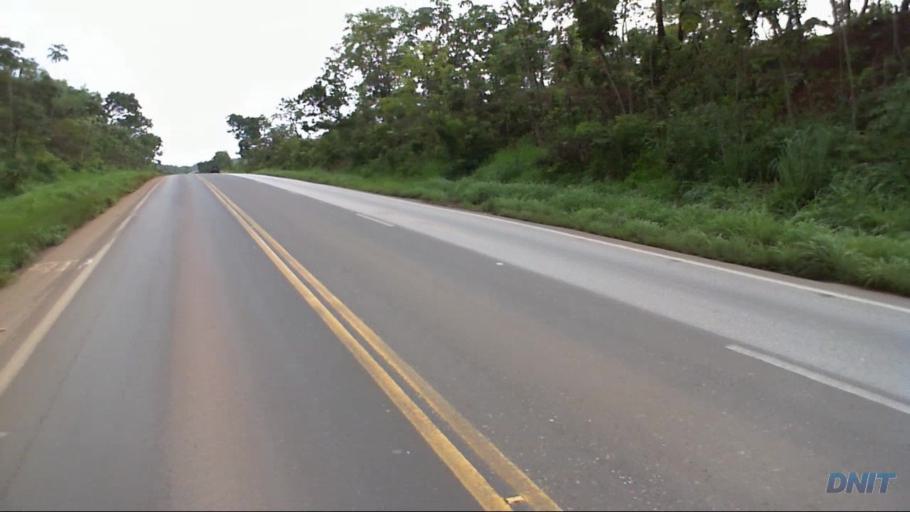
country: BR
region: Goias
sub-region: Uruacu
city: Uruacu
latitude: -14.5863
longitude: -49.1611
